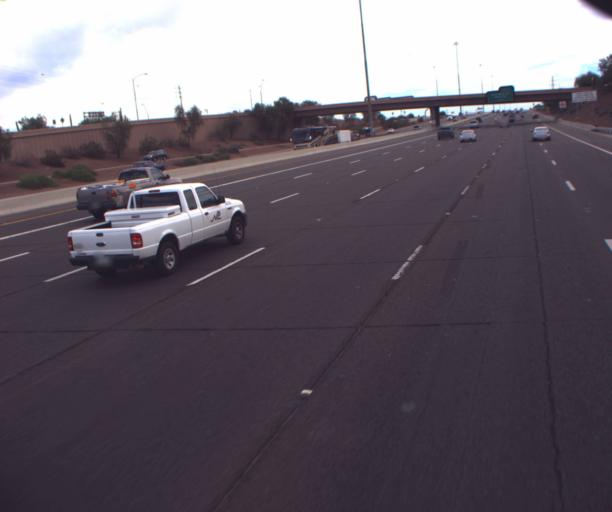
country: US
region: Arizona
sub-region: Maricopa County
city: Tempe Junction
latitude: 33.4360
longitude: -111.9515
